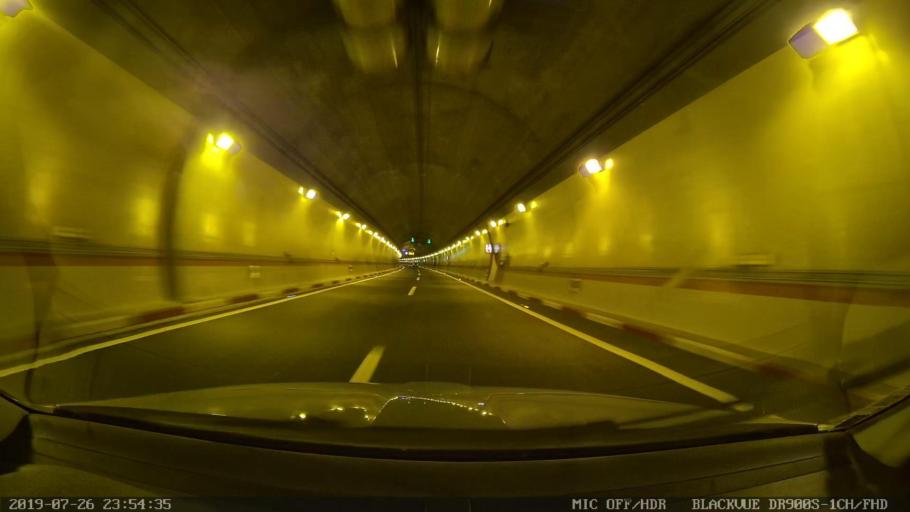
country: ES
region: Extremadura
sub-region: Provincia de Caceres
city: Higuera
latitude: 39.6919
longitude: -5.7040
